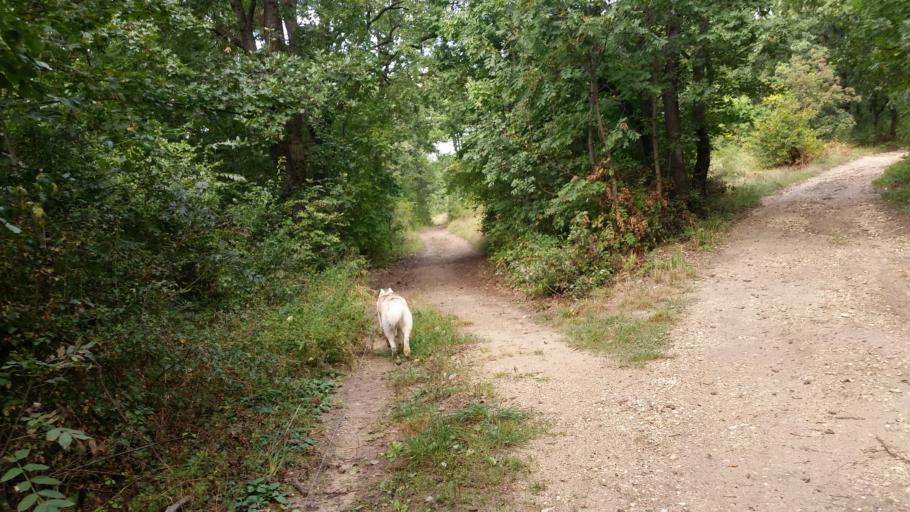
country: HU
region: Pest
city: Telki
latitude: 47.5649
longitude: 18.8220
